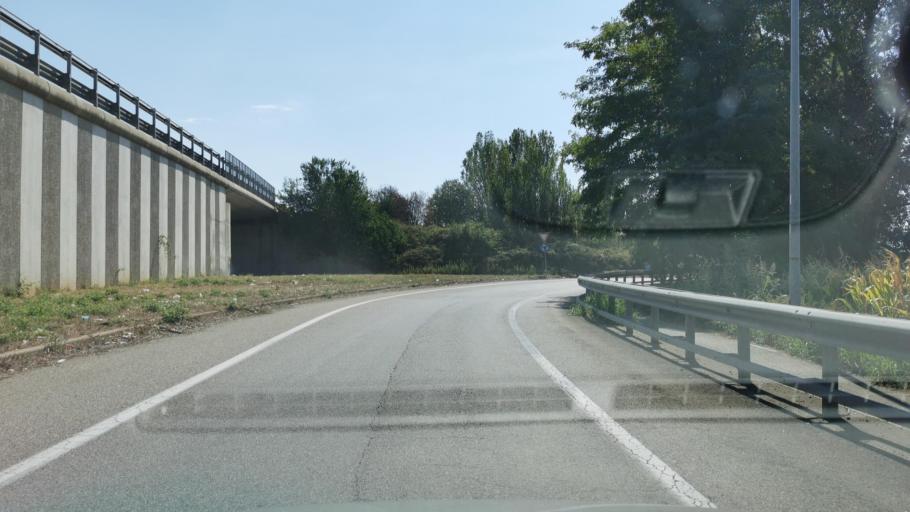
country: IT
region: Piedmont
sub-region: Provincia di Torino
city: Grugliasco
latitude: 45.0541
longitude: 7.5661
